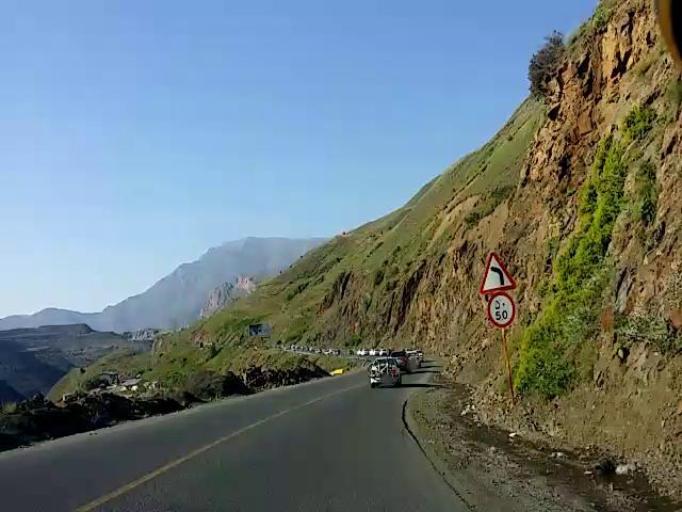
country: IR
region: Tehran
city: Tajrish
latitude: 36.1844
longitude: 51.3187
